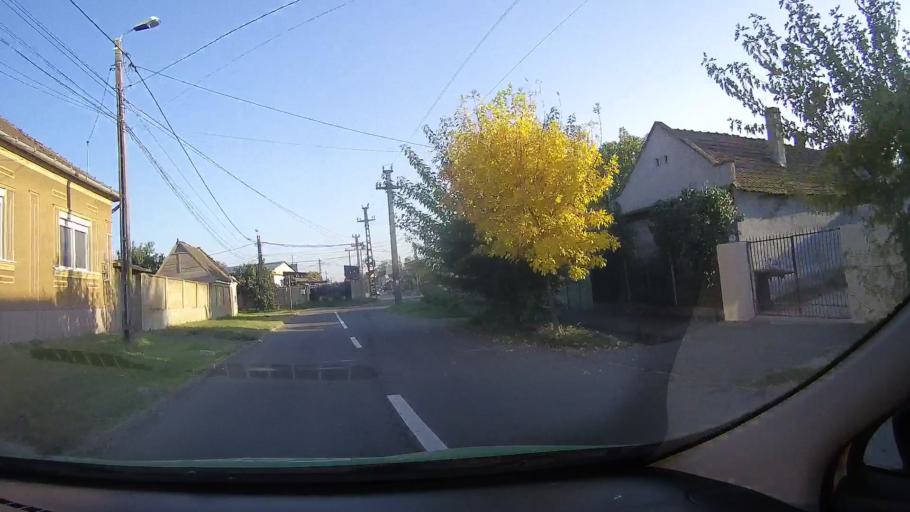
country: RO
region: Bihor
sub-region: Comuna Biharea
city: Oradea
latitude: 47.0974
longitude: 21.9005
